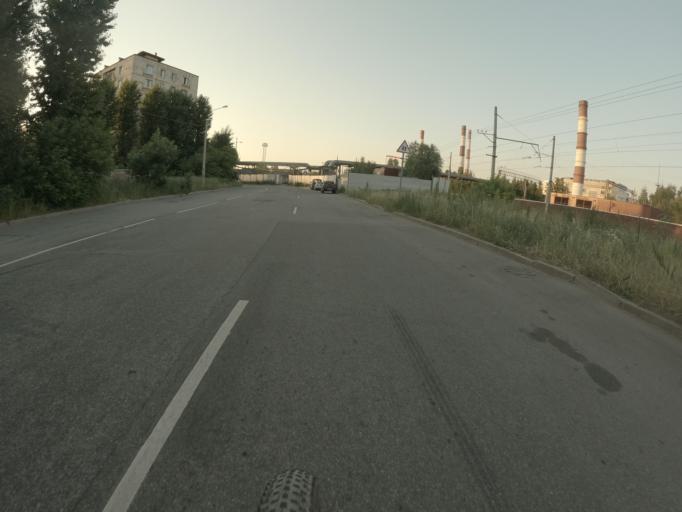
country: RU
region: St.-Petersburg
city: Avtovo
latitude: 59.8669
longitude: 30.2799
